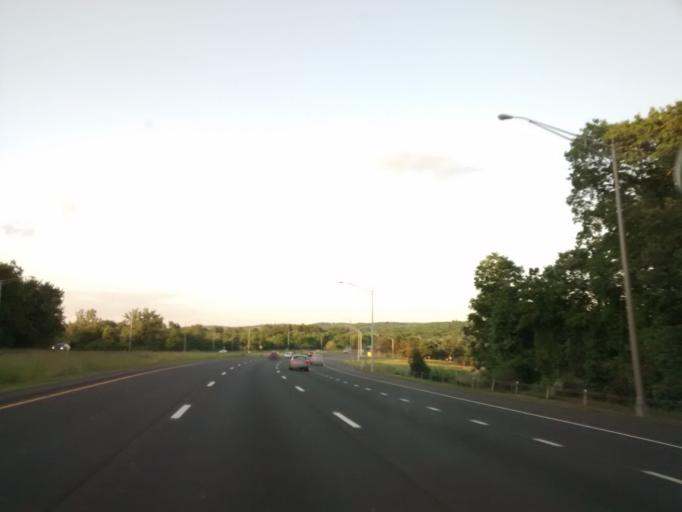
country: US
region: Connecticut
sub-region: Tolland County
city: Rockville
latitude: 41.8521
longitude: -72.4341
